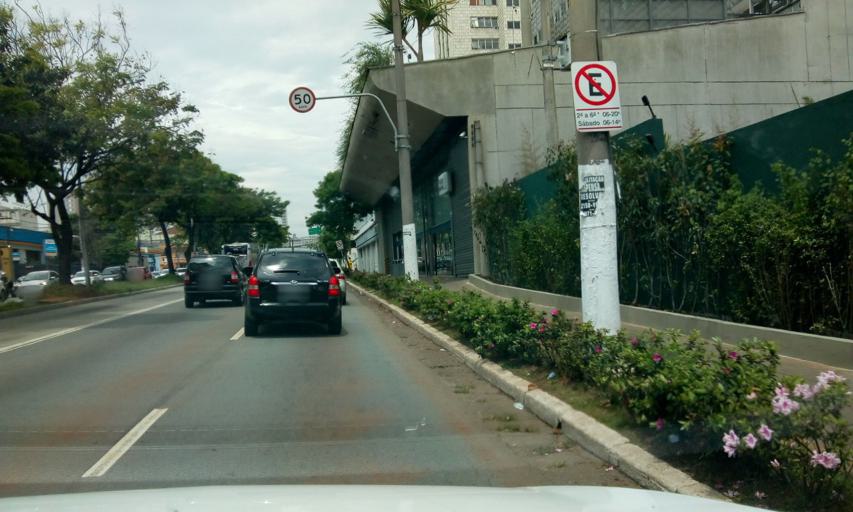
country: BR
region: Sao Paulo
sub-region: Sao Paulo
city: Sao Paulo
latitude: -23.5312
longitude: -46.6464
